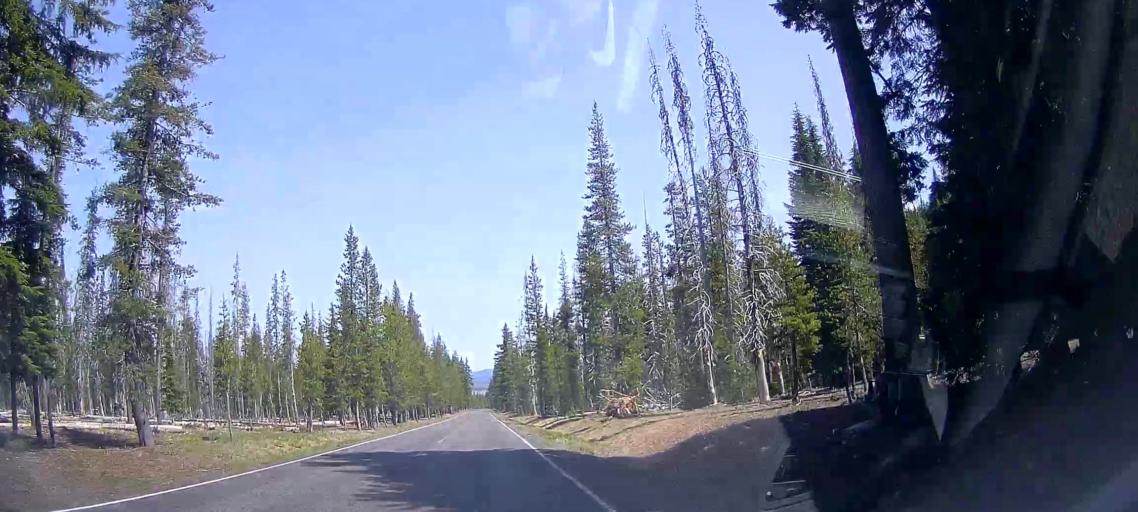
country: US
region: Oregon
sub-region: Jackson County
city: Shady Cove
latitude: 42.9976
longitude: -122.1353
